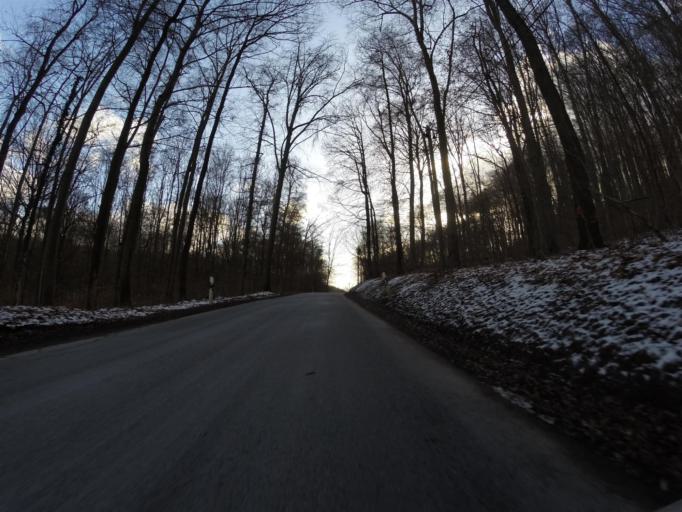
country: DE
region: Thuringia
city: Grosslobichau
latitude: 50.9388
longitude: 11.6887
